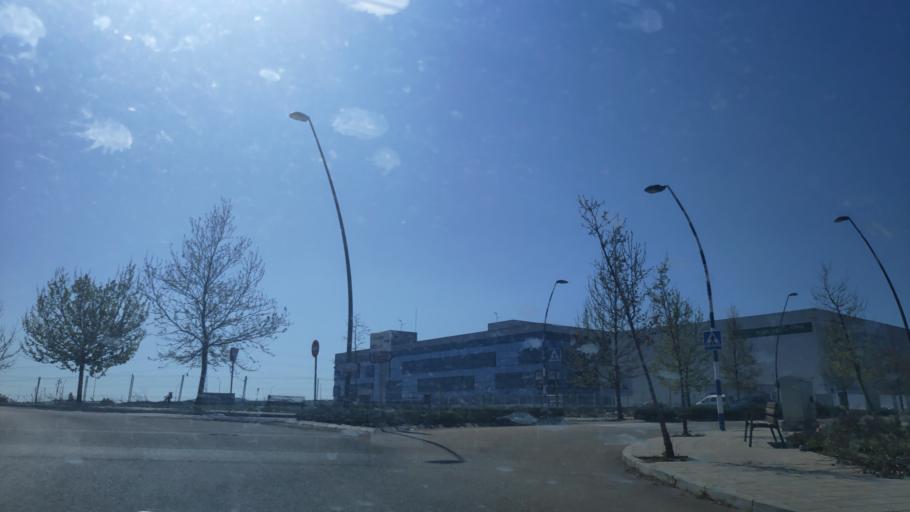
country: ES
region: Madrid
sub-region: Provincia de Madrid
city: Pinto
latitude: 40.2890
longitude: -3.6811
